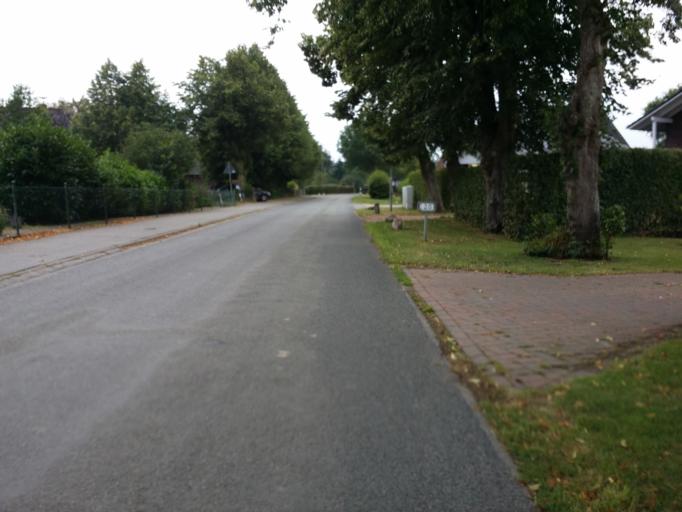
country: DE
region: Schleswig-Holstein
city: Heiligenstedtenerkamp
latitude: 53.8952
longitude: 9.4653
